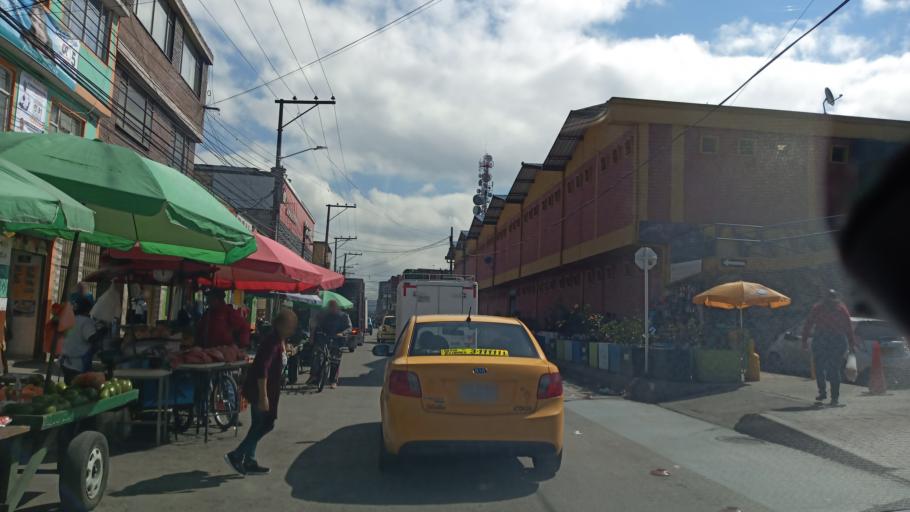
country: CO
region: Cundinamarca
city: Funza
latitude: 4.6760
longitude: -74.1450
